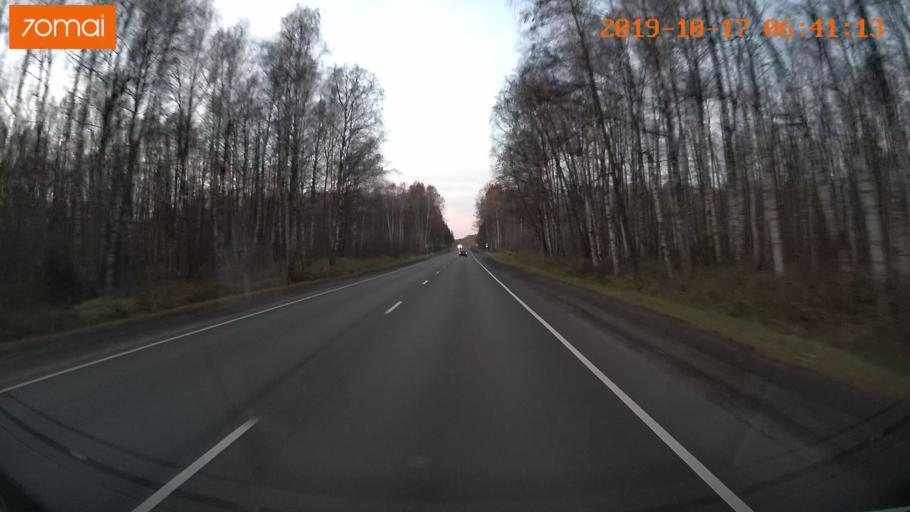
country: RU
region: Ivanovo
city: Nerl'
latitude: 56.6180
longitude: 40.5622
